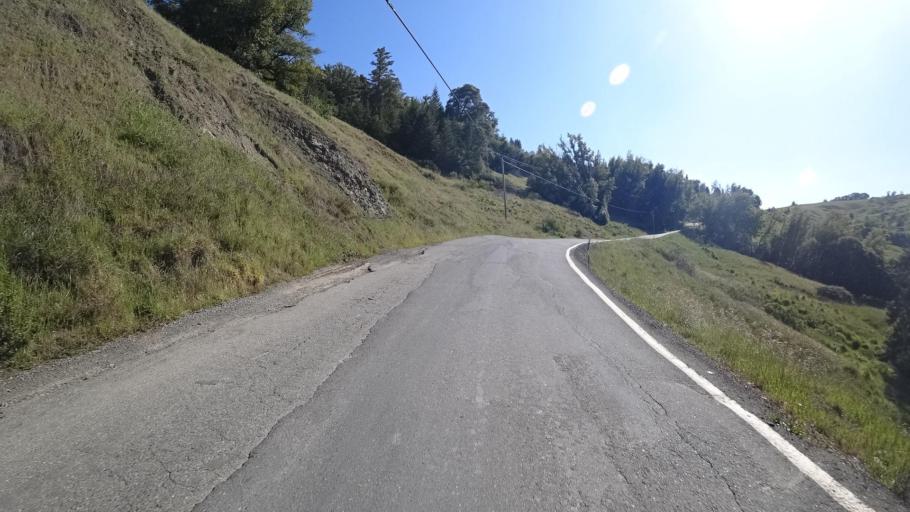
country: US
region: California
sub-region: Humboldt County
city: Redway
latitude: 40.1145
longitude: -123.7624
